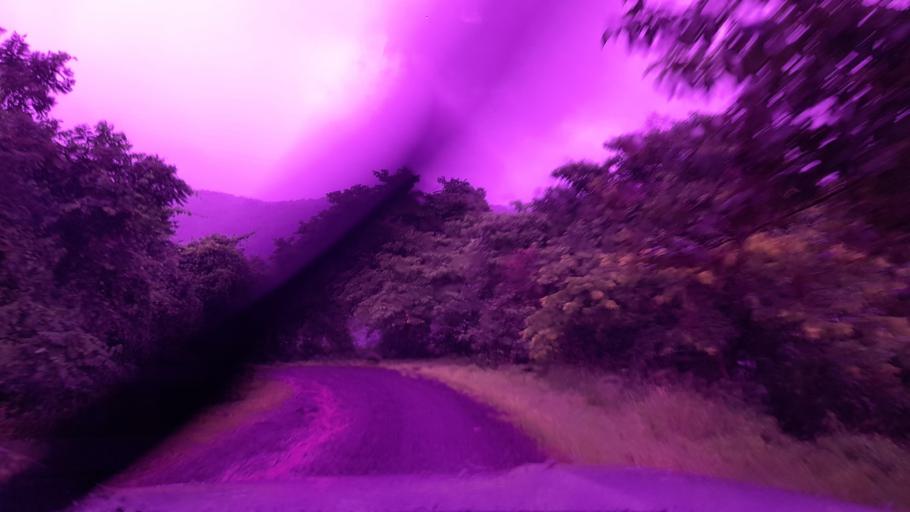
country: ET
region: Oromiya
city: Metu
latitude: 8.4797
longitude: 35.6432
